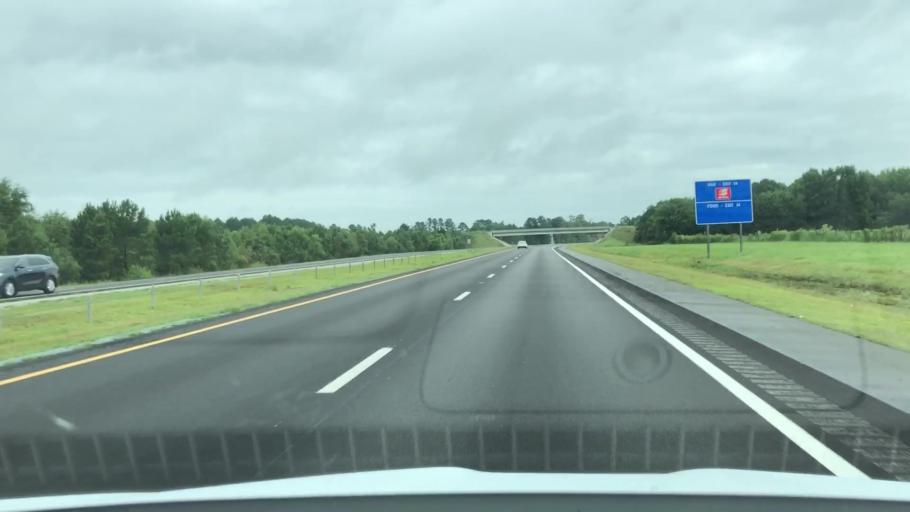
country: US
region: North Carolina
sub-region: Wayne County
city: Fremont
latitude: 35.5357
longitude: -77.9898
